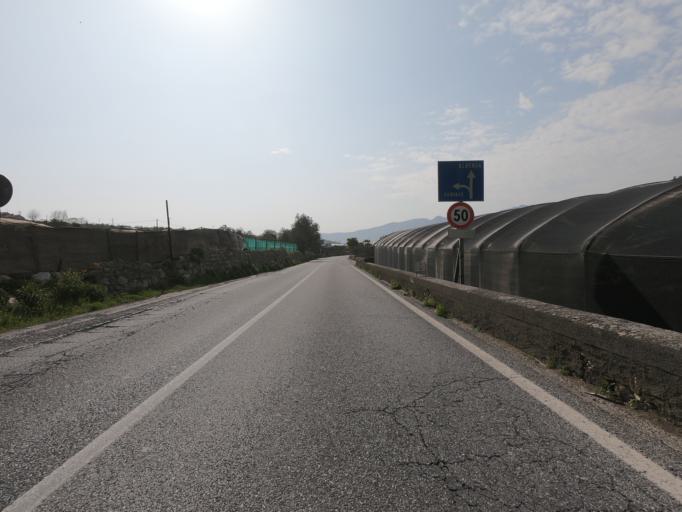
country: IT
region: Liguria
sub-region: Provincia di Savona
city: Cisano
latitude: 44.0812
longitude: 8.1555
